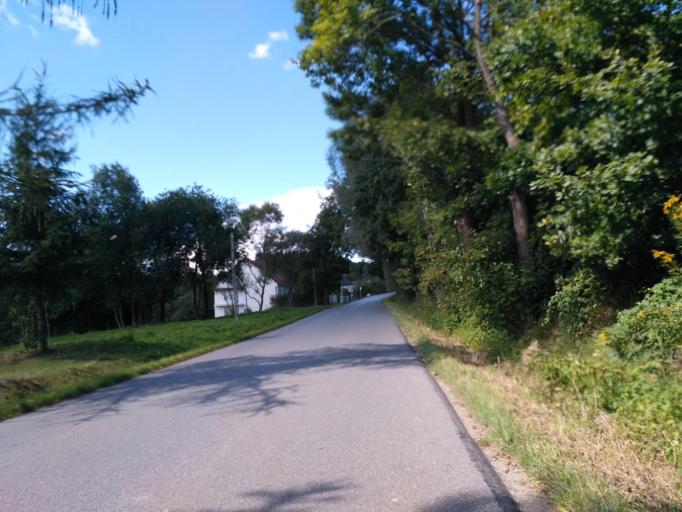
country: PL
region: Subcarpathian Voivodeship
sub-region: Powiat jasielski
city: Skolyszyn
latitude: 49.7819
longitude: 21.3536
